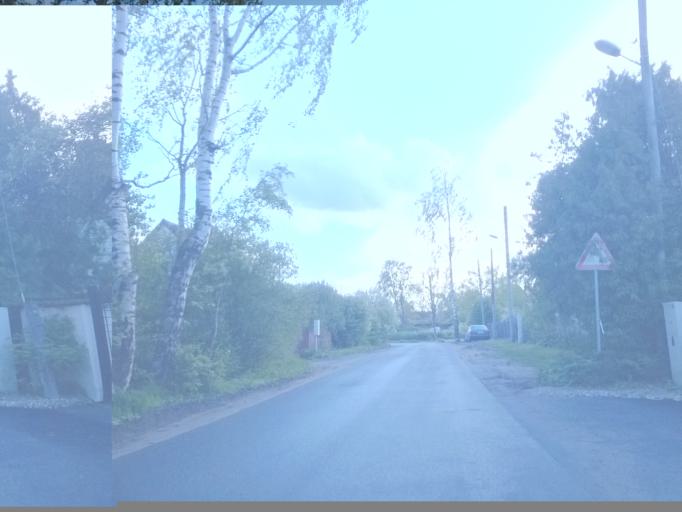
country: LV
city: Tireli
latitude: 56.9506
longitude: 23.6256
